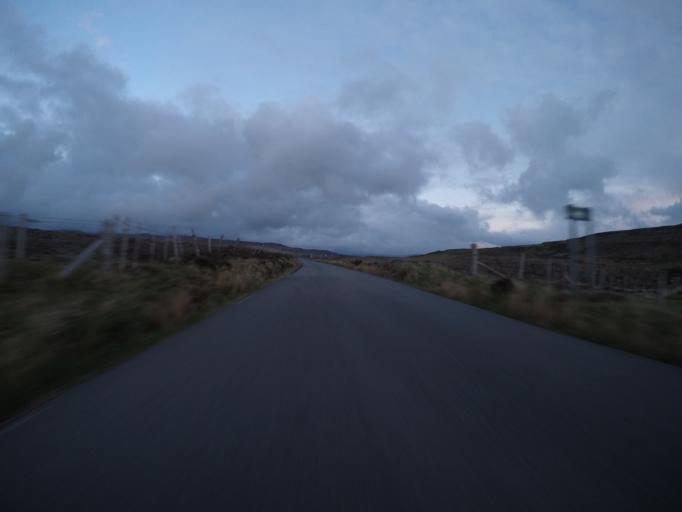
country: GB
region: Scotland
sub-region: Highland
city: Portree
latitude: 57.5974
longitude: -6.3755
